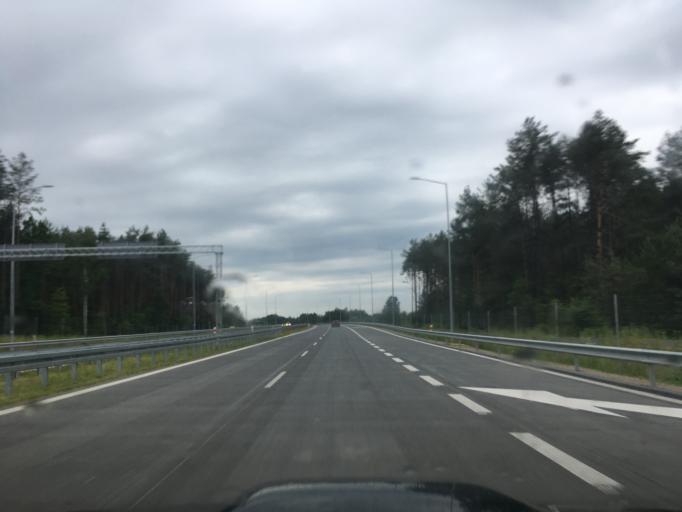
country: PL
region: Masovian Voivodeship
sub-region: Powiat piaseczynski
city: Gora Kalwaria
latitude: 51.9740
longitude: 21.1913
